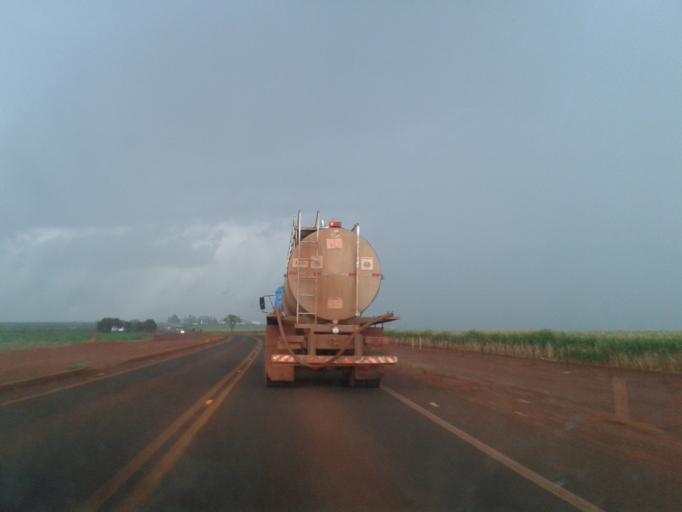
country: BR
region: Goias
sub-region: Quirinopolis
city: Quirinopolis
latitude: -18.5676
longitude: -50.4379
